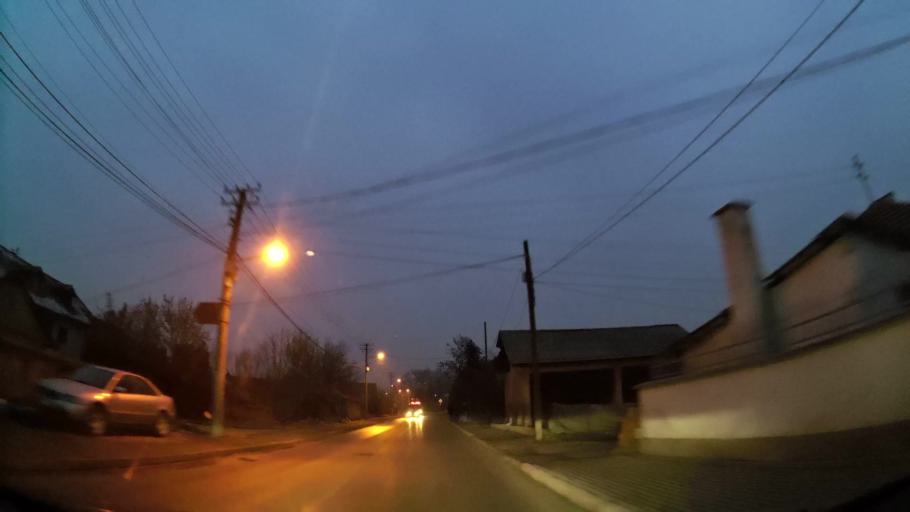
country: MK
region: Kisela Voda
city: Kisela Voda
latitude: 41.9684
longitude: 21.4883
